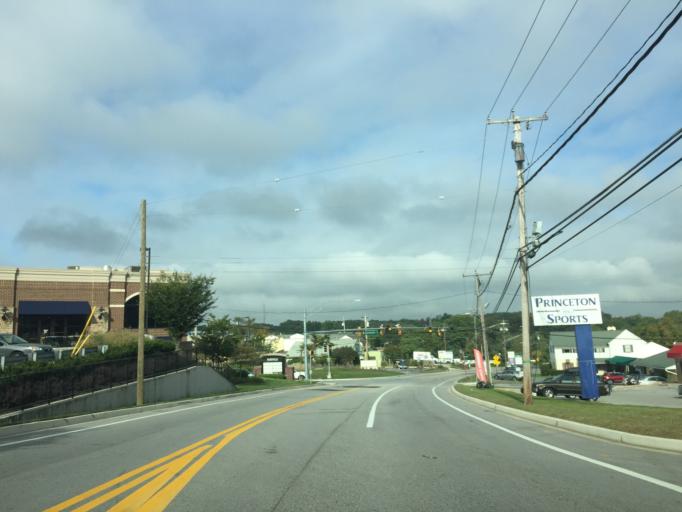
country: US
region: Maryland
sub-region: Baltimore County
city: Lutherville
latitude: 39.3830
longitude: -76.6564
